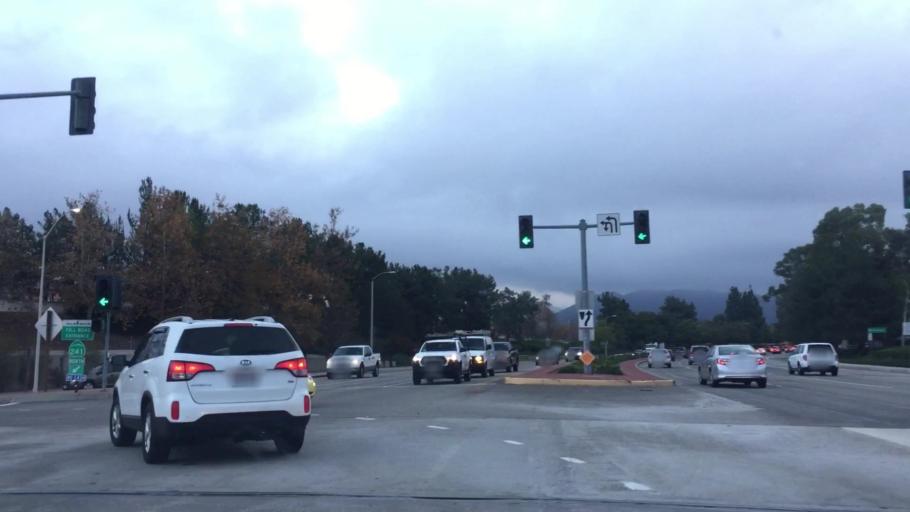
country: US
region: California
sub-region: Orange County
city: Rancho Santa Margarita
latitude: 33.6432
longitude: -117.6041
